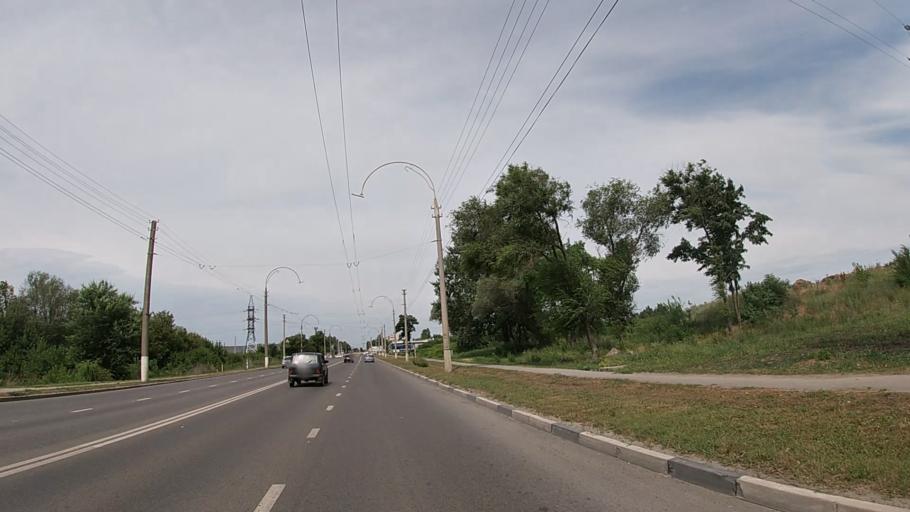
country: RU
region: Belgorod
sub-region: Belgorodskiy Rayon
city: Belgorod
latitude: 50.6112
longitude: 36.5408
